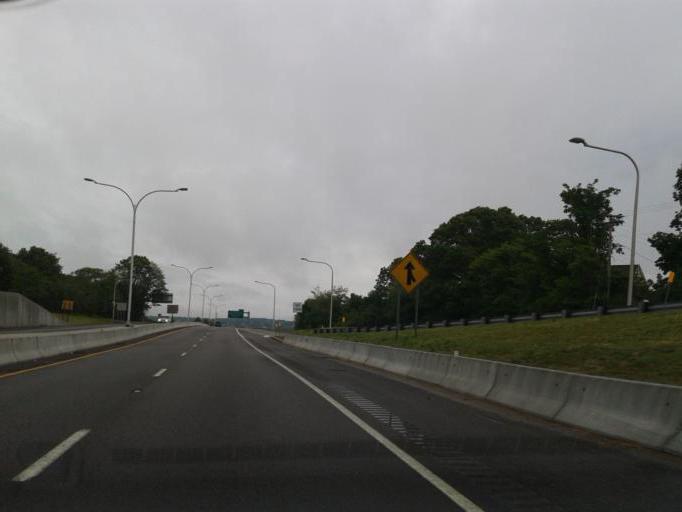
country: US
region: Rhode Island
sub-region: Newport County
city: Tiverton
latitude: 41.6408
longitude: -71.2049
